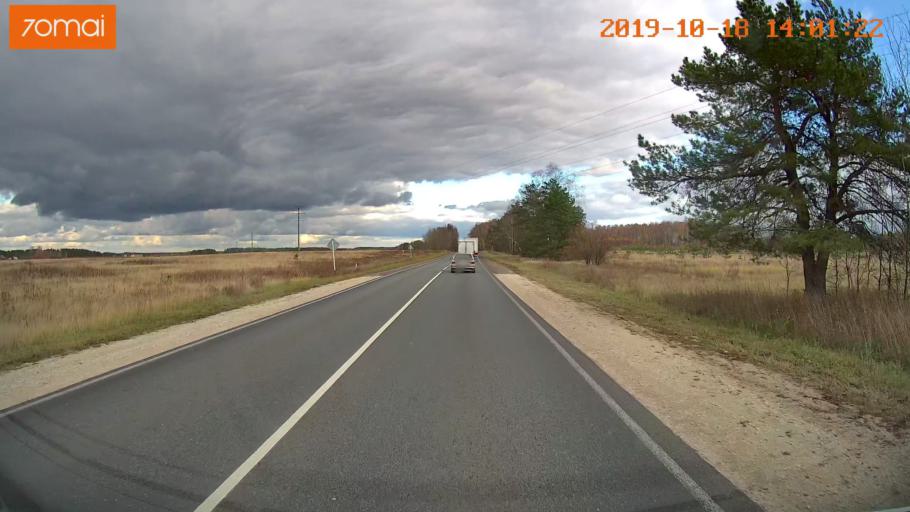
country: RU
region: Rjazan
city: Spas-Klepiki
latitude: 55.1069
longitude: 40.0881
